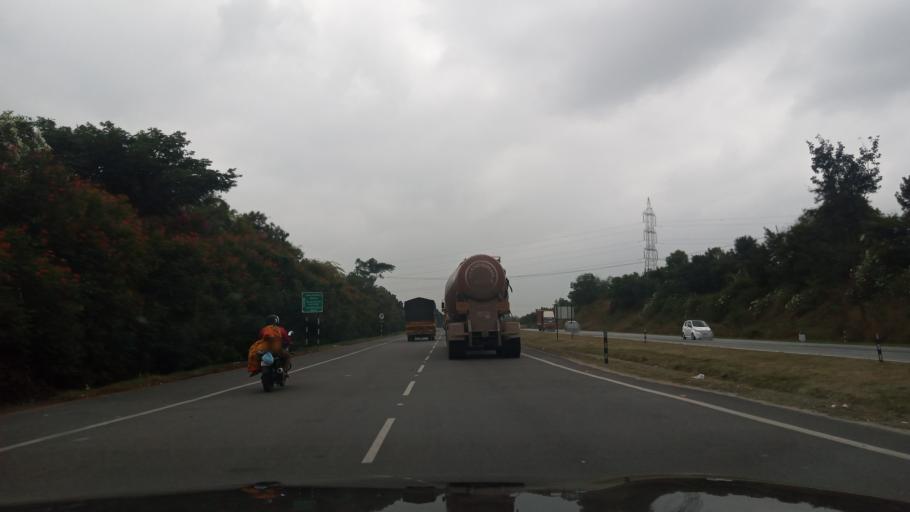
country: IN
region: Karnataka
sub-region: Bangalore Rural
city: Nelamangala
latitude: 13.0402
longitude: 77.4757
